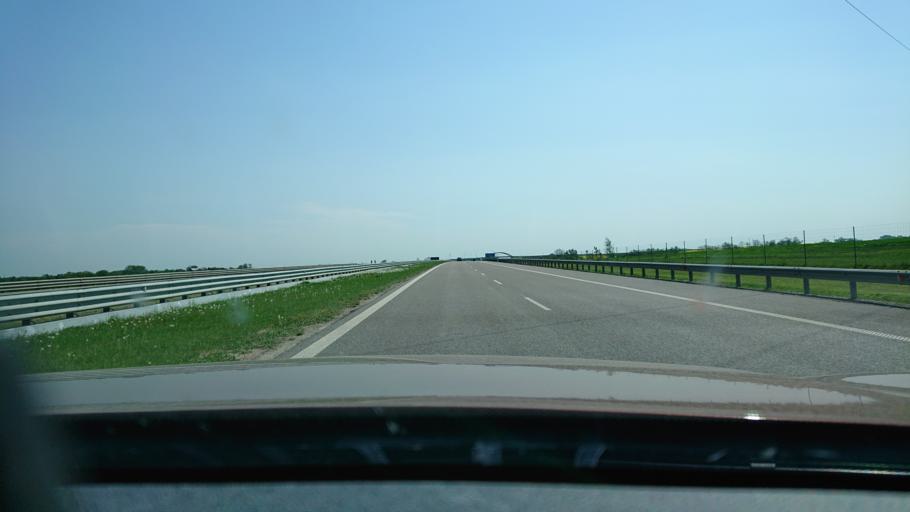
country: PL
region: Subcarpathian Voivodeship
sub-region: Powiat przemyski
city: Orly
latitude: 49.9145
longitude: 22.7892
